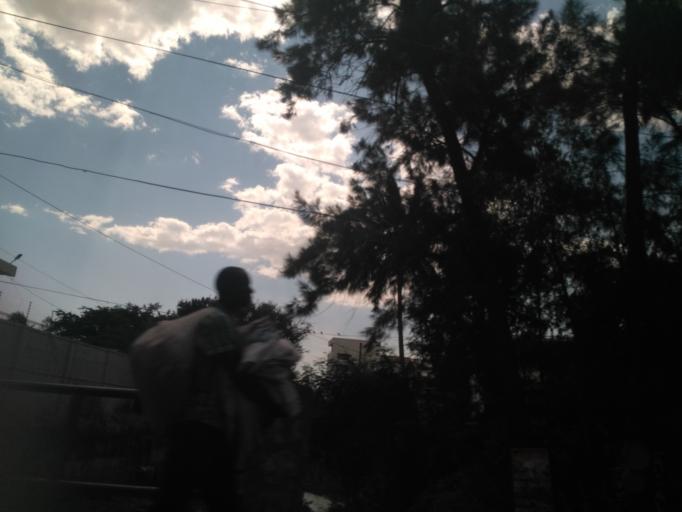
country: TZ
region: Mwanza
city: Mwanza
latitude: -2.5162
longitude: 32.9013
